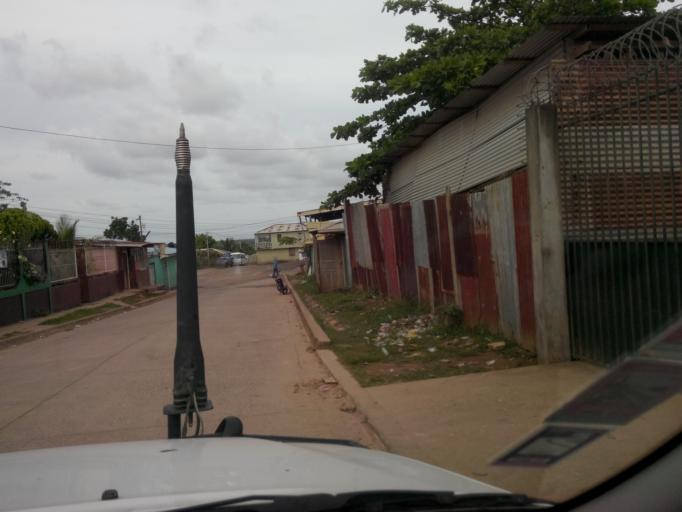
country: NI
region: Atlantico Sur
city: Bluefields
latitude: 12.0282
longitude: -83.7706
